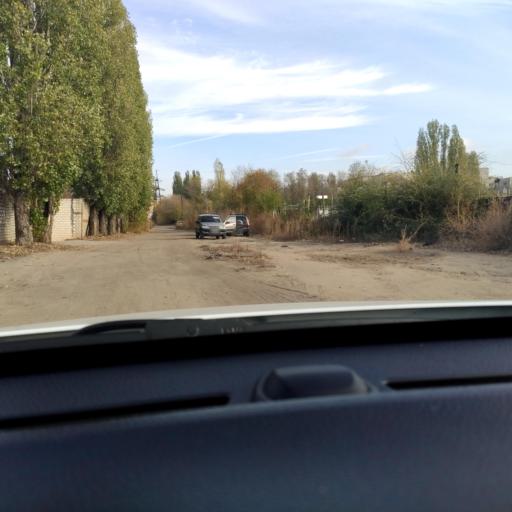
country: RU
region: Voronezj
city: Voronezh
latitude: 51.6374
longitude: 39.1521
